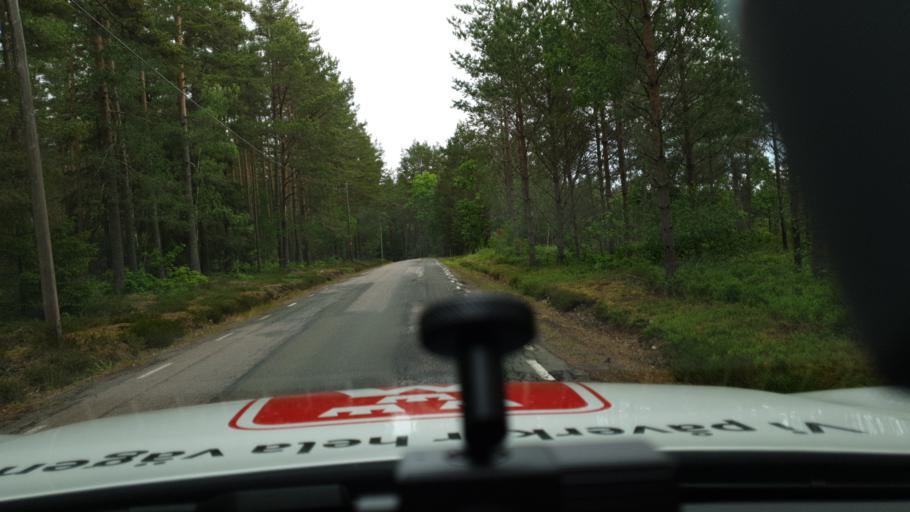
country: SE
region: Vaestra Goetaland
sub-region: Karlsborgs Kommun
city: Molltorp
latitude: 58.4246
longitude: 14.3722
